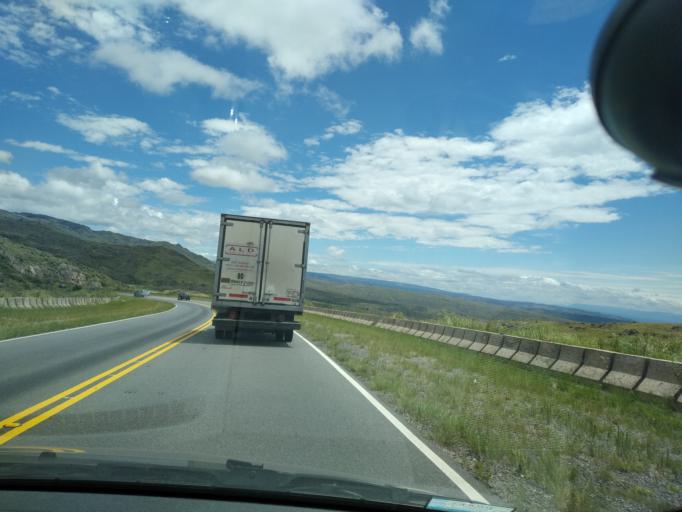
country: AR
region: Cordoba
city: Cuesta Blanca
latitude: -31.6175
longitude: -64.6692
